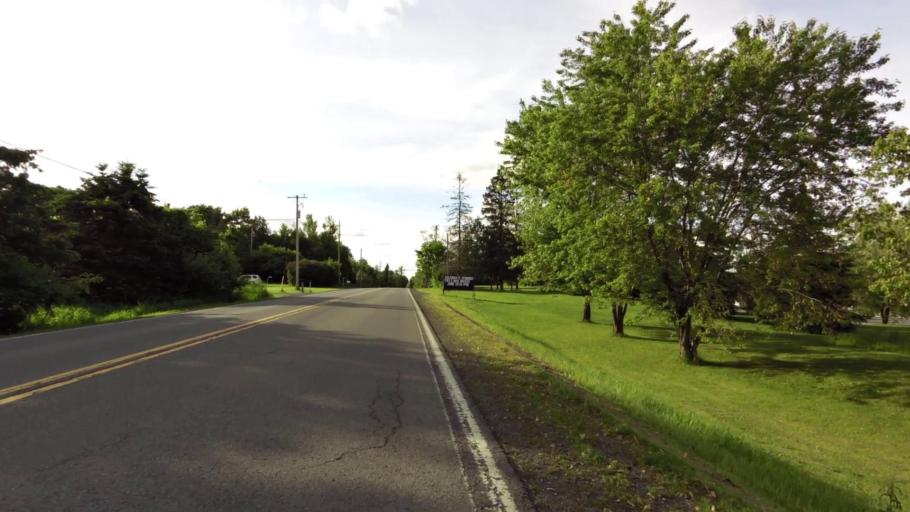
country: CA
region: Ontario
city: Ottawa
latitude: 45.2341
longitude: -75.6108
